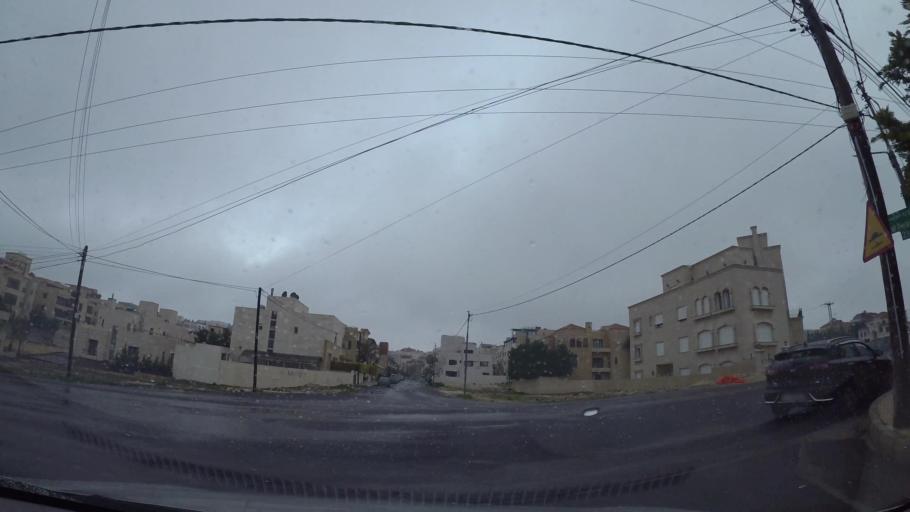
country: JO
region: Amman
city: Al Jubayhah
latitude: 32.0049
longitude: 35.8233
